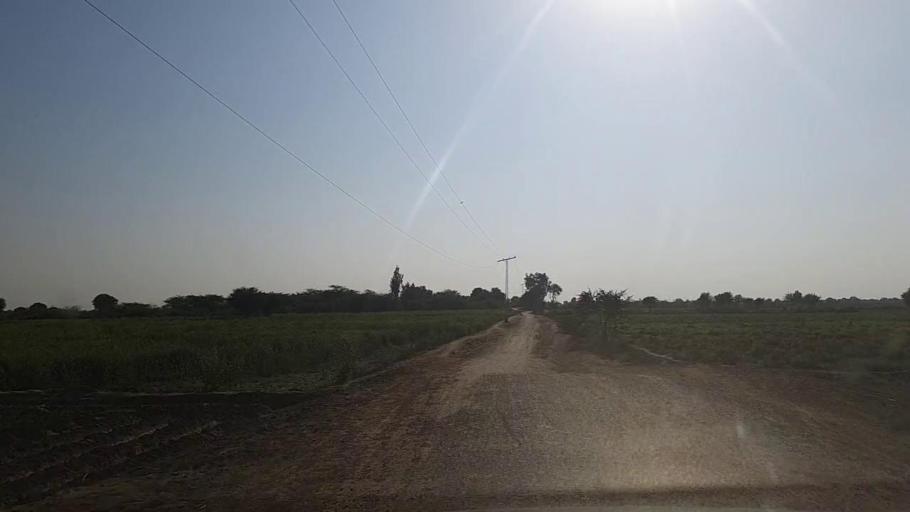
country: PK
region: Sindh
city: Digri
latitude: 25.0218
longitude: 69.2268
